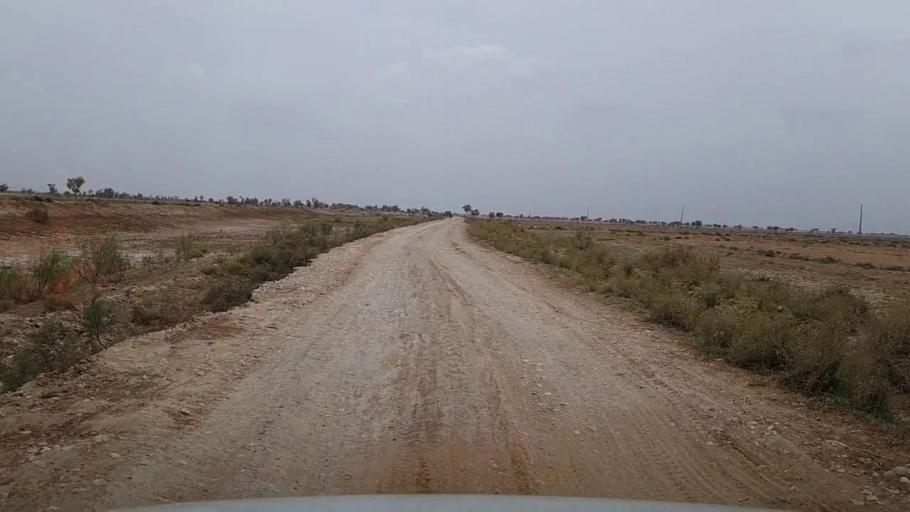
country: PK
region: Sindh
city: Sehwan
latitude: 26.3584
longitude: 67.7979
